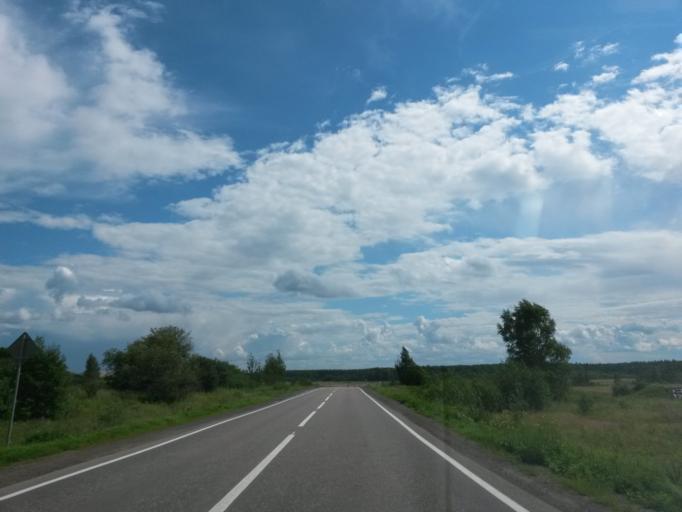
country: RU
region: Jaroslavl
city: Gavrilov-Yam
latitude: 57.3051
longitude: 39.9429
